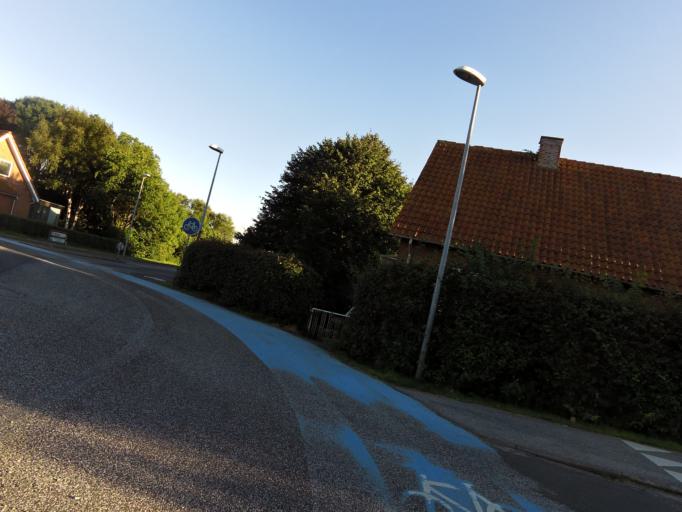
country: DK
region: South Denmark
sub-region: Esbjerg Kommune
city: Ribe
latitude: 55.3372
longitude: 8.7760
